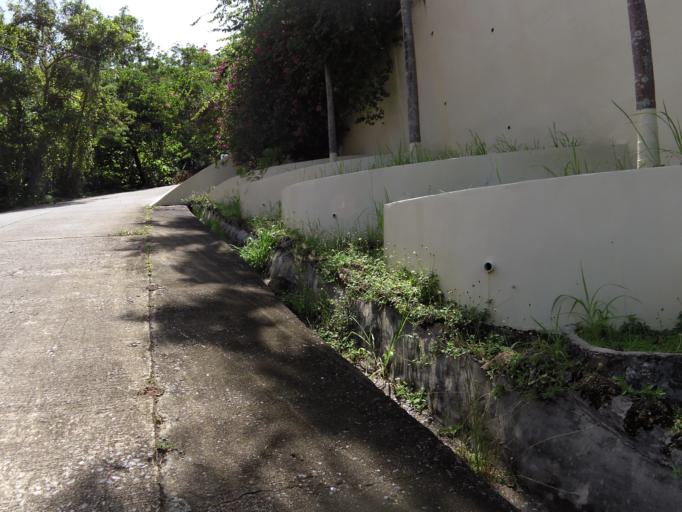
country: TH
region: Phuket
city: Ban Karon
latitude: 7.8471
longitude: 98.3015
